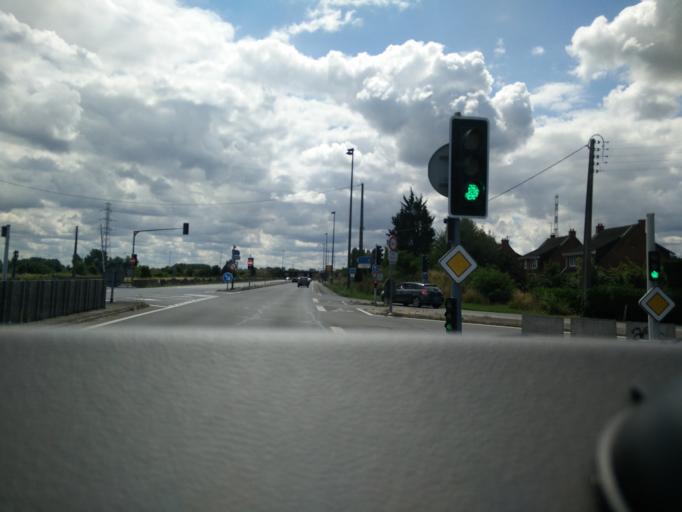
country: FR
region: Nord-Pas-de-Calais
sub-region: Departement du Nord
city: Coudekerque-Branche
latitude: 51.0316
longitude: 2.4063
